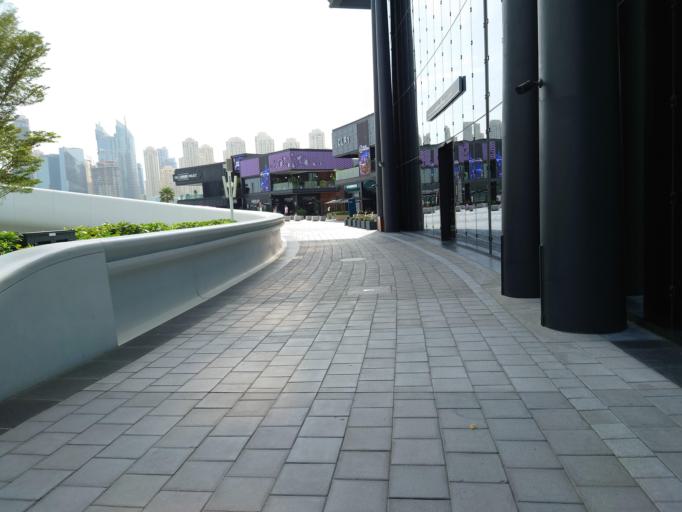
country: AE
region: Dubai
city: Dubai
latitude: 25.0795
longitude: 55.1234
